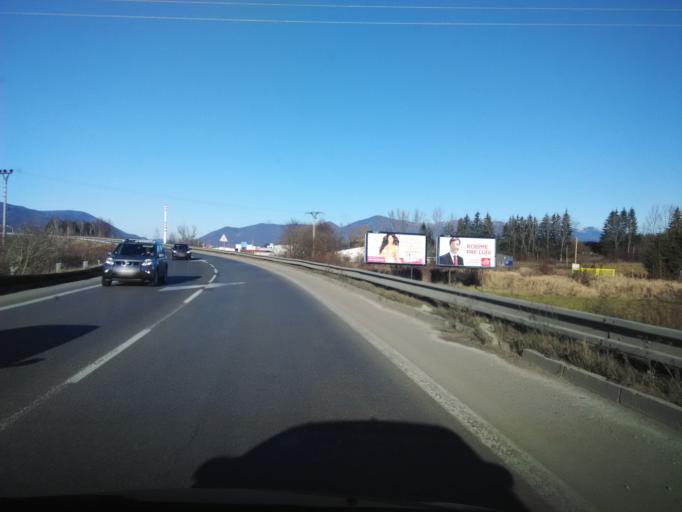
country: SK
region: Zilinsky
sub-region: Okres Martin
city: Martin
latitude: 49.0404
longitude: 18.9114
